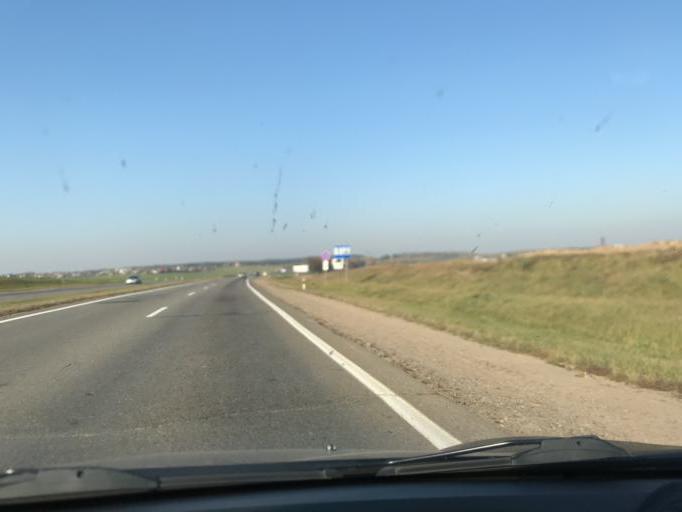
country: BY
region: Minsk
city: Luhavaya Slabada
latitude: 53.7479
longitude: 27.8356
